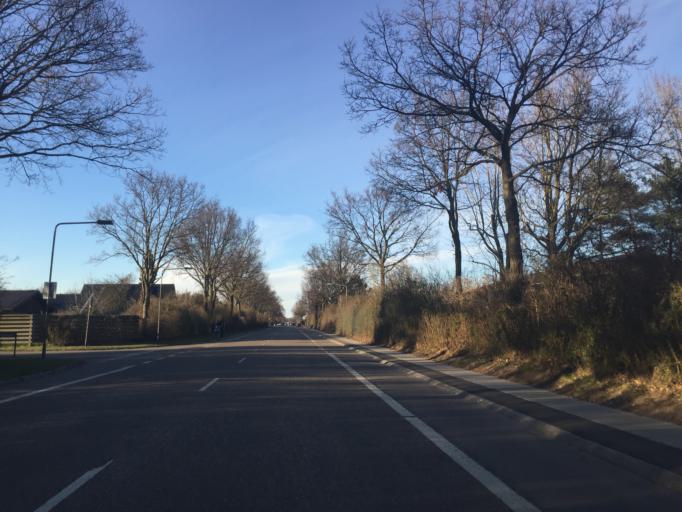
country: DK
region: Capital Region
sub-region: Dragor Kommune
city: Dragor
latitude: 55.5927
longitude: 12.6577
